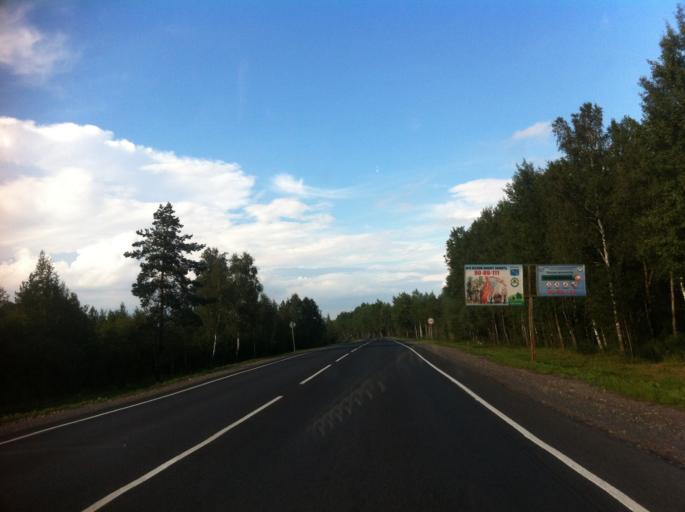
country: RU
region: Leningrad
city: Luga
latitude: 58.4383
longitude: 29.7495
